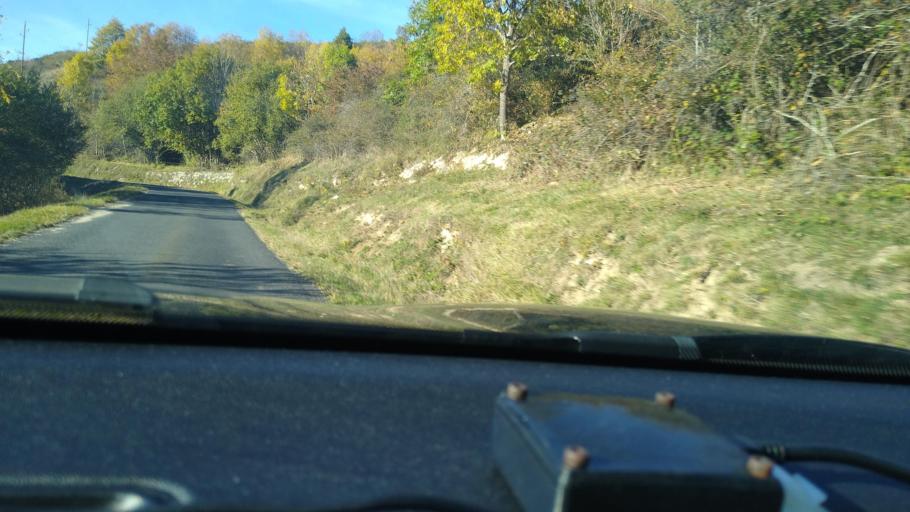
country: FR
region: Languedoc-Roussillon
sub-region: Departement de l'Aude
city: Quillan
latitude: 42.7282
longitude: 2.1189
